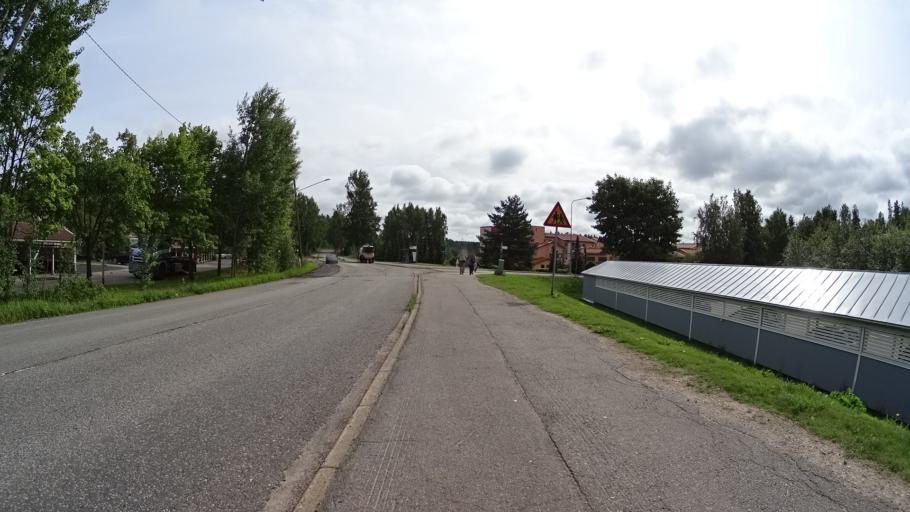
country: FI
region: Uusimaa
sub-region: Helsinki
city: Kauniainen
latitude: 60.2058
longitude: 24.7346
